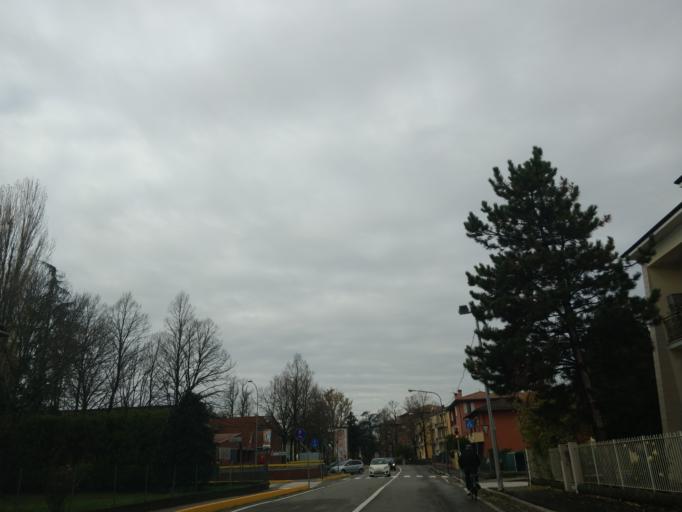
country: IT
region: Emilia-Romagna
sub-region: Provincia di Bologna
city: Pieve di Cento
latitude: 44.7108
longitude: 11.3098
